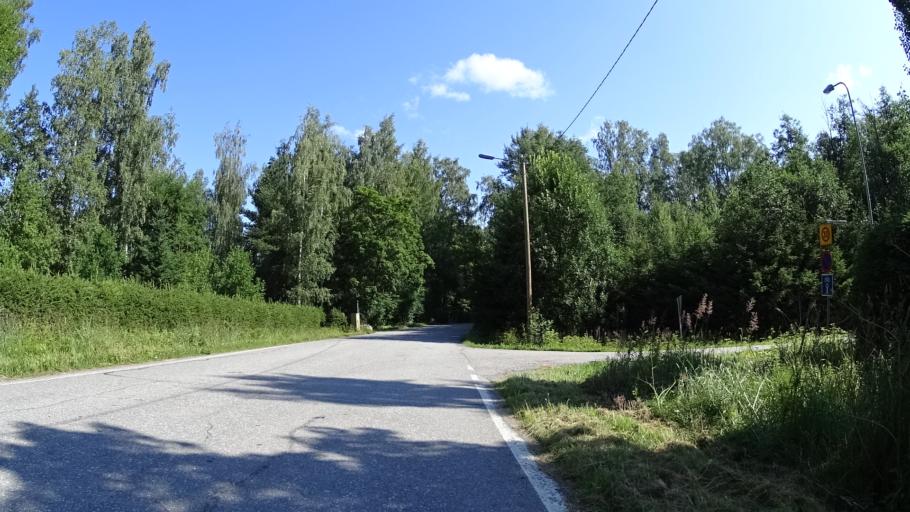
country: FI
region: Uusimaa
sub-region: Helsinki
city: Jaervenpaeae
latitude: 60.4359
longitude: 25.0614
